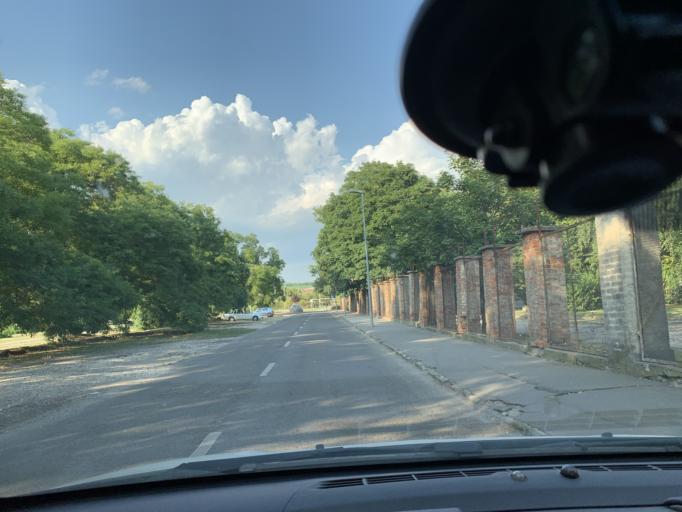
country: HU
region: Pest
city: Vac
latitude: 47.7722
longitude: 19.1481
